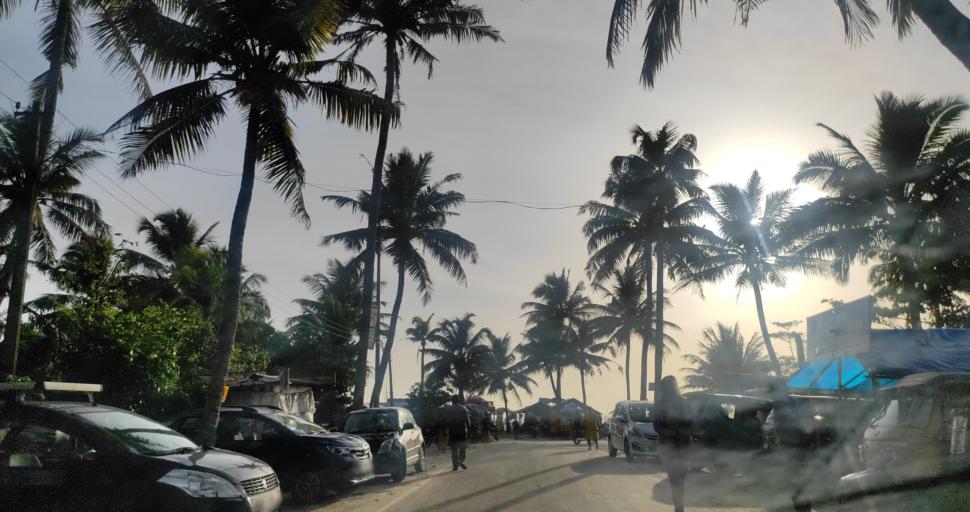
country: IN
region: Kerala
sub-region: Alappuzha
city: Shertallai
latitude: 9.6015
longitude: 76.2992
